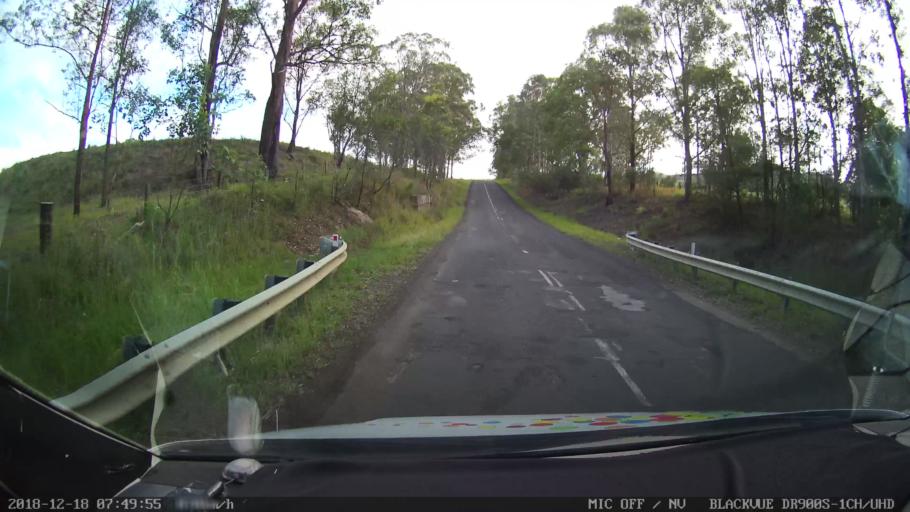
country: AU
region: New South Wales
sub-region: Kyogle
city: Kyogle
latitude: -28.4498
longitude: 152.5721
